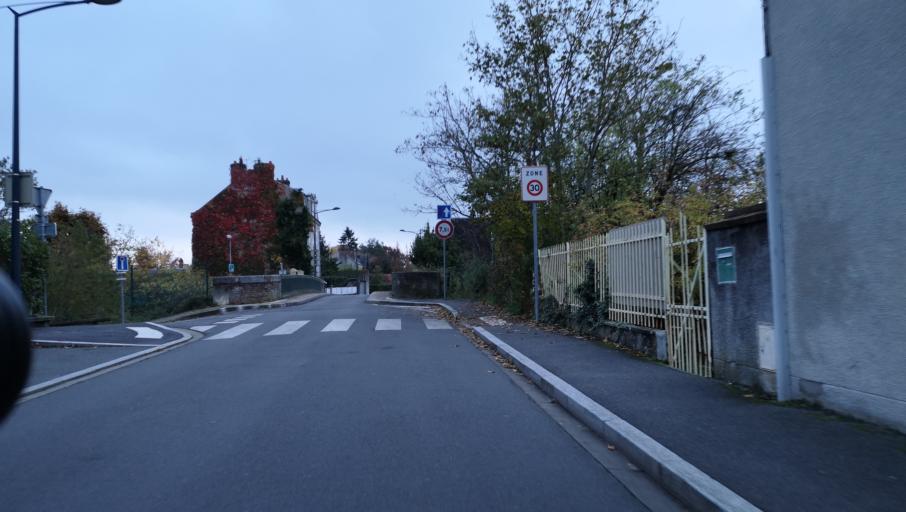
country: FR
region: Centre
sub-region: Departement du Loiret
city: Saint-Jean-le-Blanc
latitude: 47.9082
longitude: 1.9245
